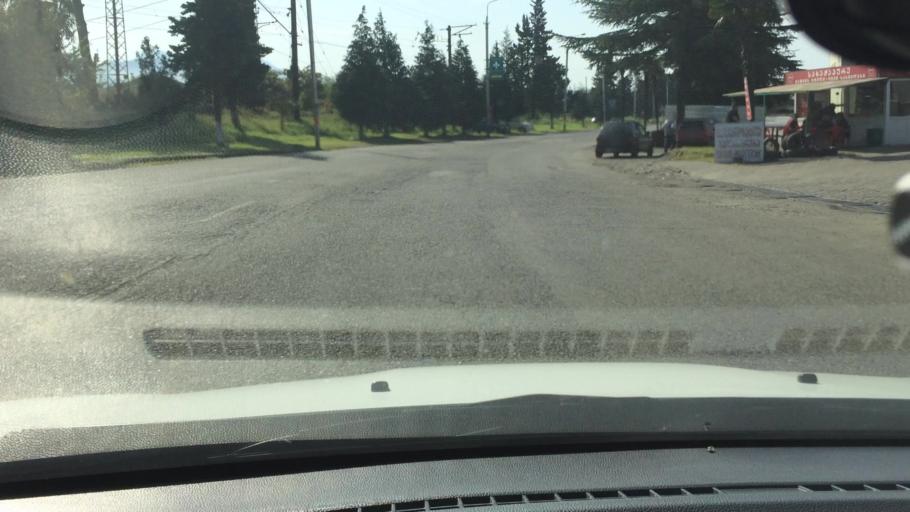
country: GE
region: Ajaria
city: Kobuleti
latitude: 41.8068
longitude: 41.7780
